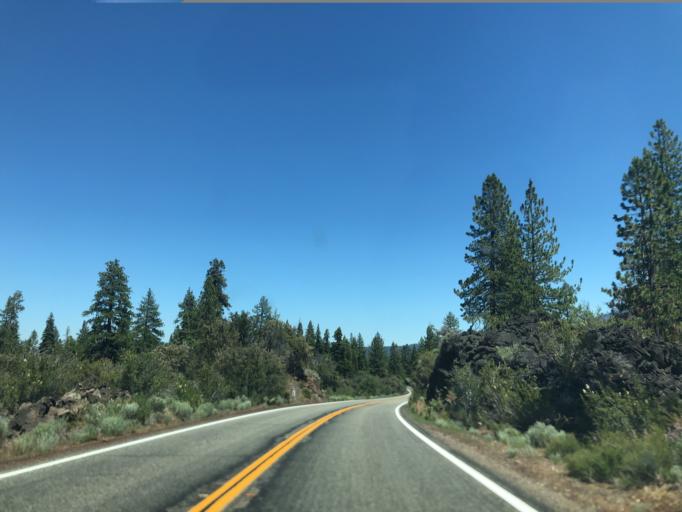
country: US
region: California
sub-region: Shasta County
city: Burney
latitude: 40.6175
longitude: -121.4965
